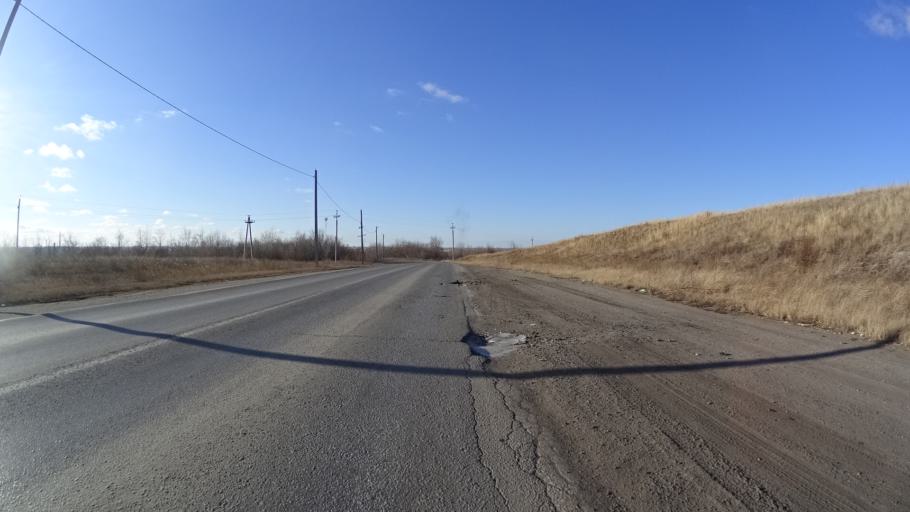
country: RU
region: Chelyabinsk
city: Troitsk
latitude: 54.0805
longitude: 61.6053
